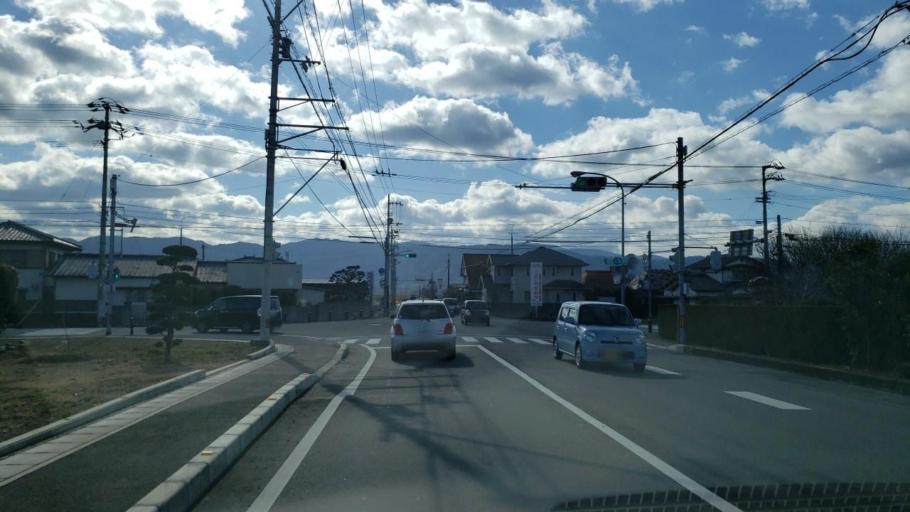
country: JP
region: Tokushima
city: Kamojimacho-jogejima
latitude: 34.0964
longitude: 134.3443
